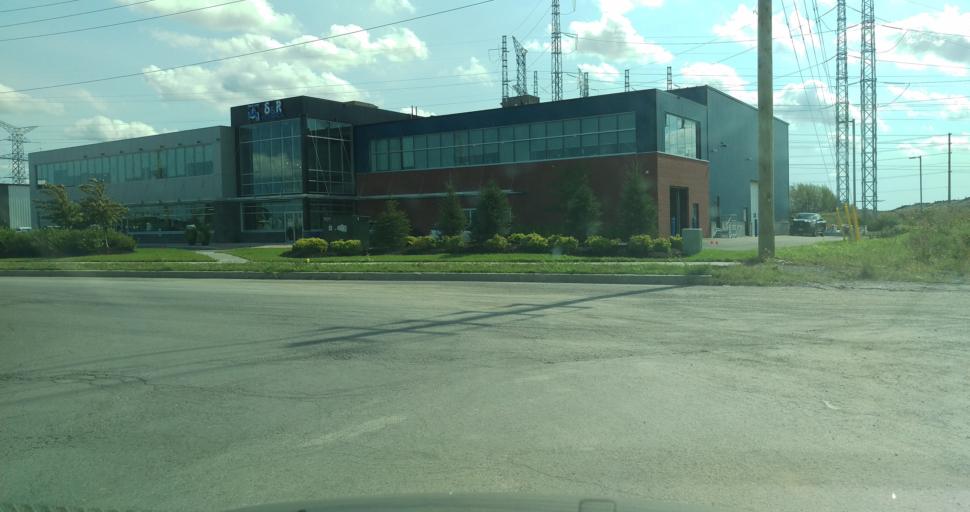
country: CA
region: Quebec
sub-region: Outaouais
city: Gatineau
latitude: 45.4563
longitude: -75.4914
